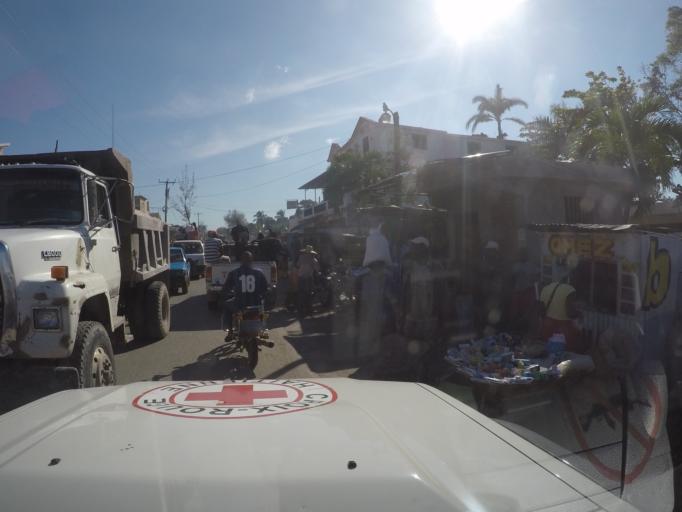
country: HT
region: Ouest
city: Grangwav
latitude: 18.4262
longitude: -72.7148
